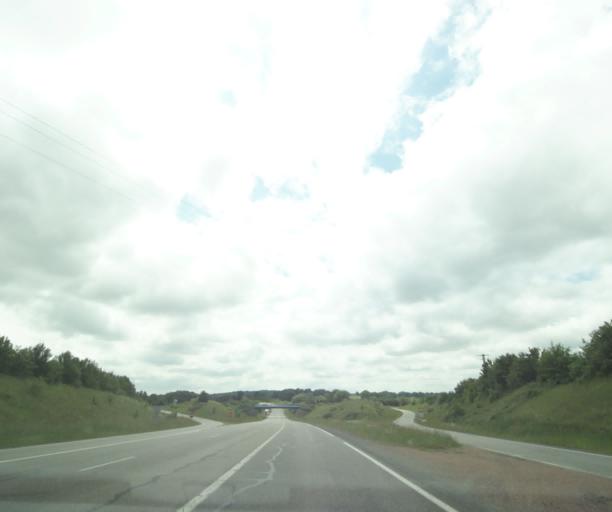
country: FR
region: Poitou-Charentes
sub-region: Departement des Deux-Sevres
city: Le Tallud
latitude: 46.6408
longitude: -0.2766
